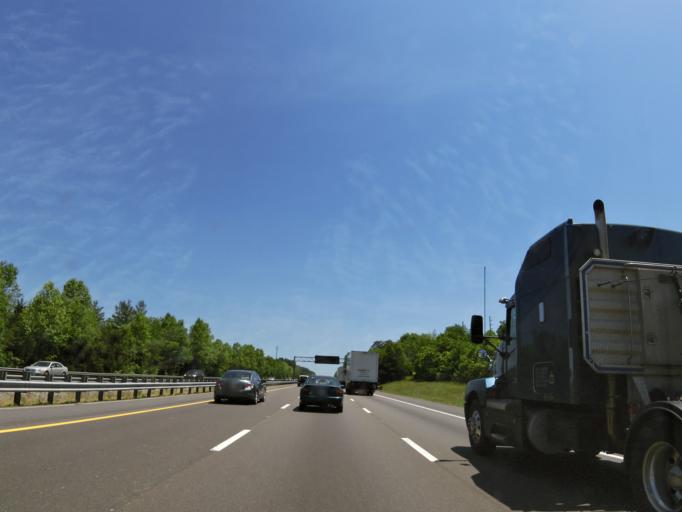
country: US
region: Tennessee
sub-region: Jefferson County
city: Dandridge
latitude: 36.0189
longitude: -83.4913
